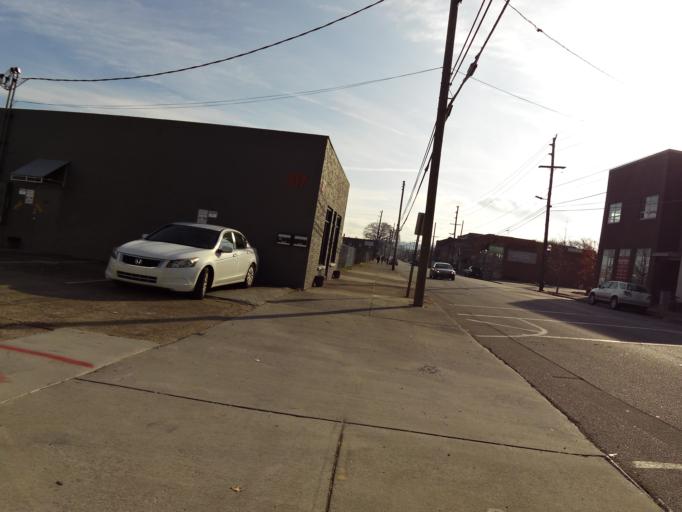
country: US
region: Tennessee
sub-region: Hamilton County
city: Chattanooga
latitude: 35.0349
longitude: -85.3039
